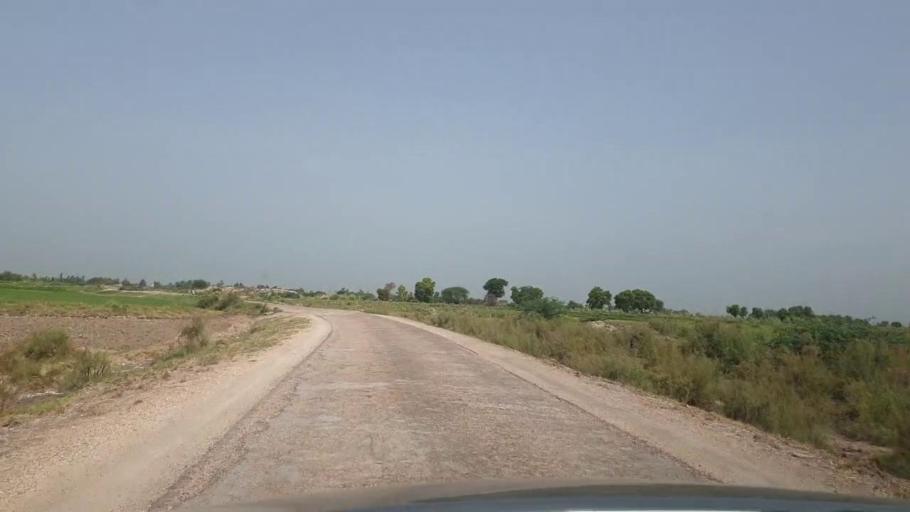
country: PK
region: Sindh
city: Madeji
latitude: 27.8394
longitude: 68.4416
